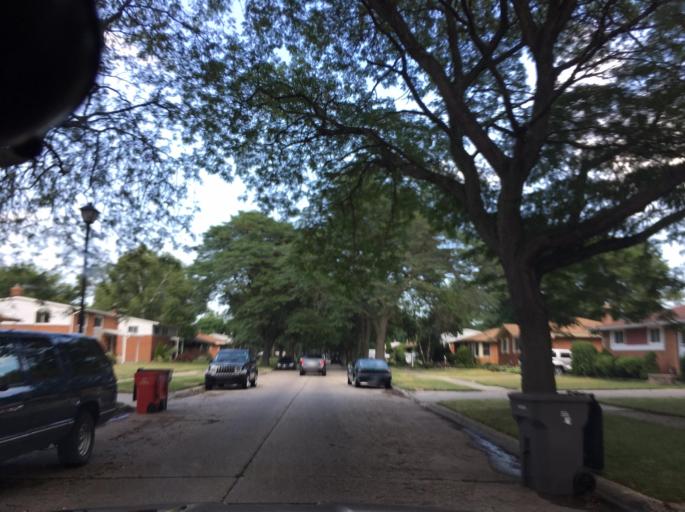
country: US
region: Michigan
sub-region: Macomb County
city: Clinton
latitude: 42.5641
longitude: -82.9100
